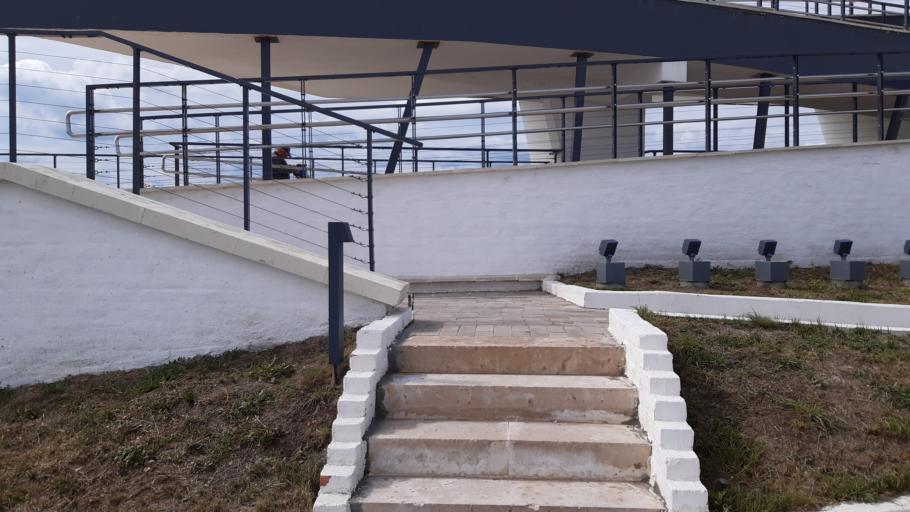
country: RU
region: Tula
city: Kurkino
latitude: 53.6247
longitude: 38.6726
